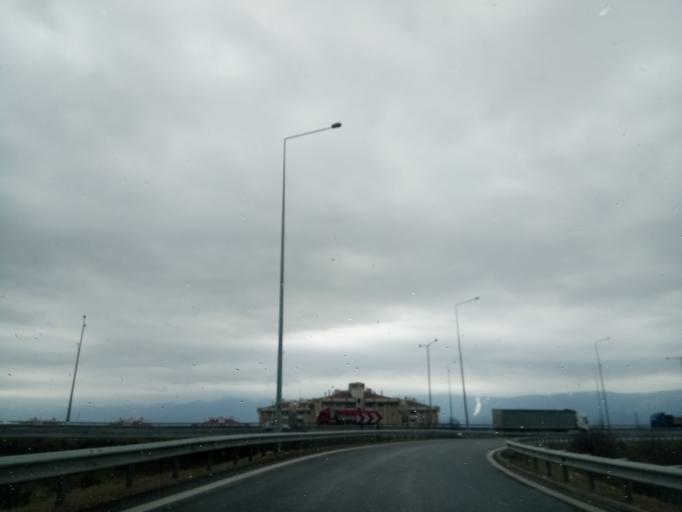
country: TR
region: Bolu
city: Bolu
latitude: 40.7170
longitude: 31.5220
